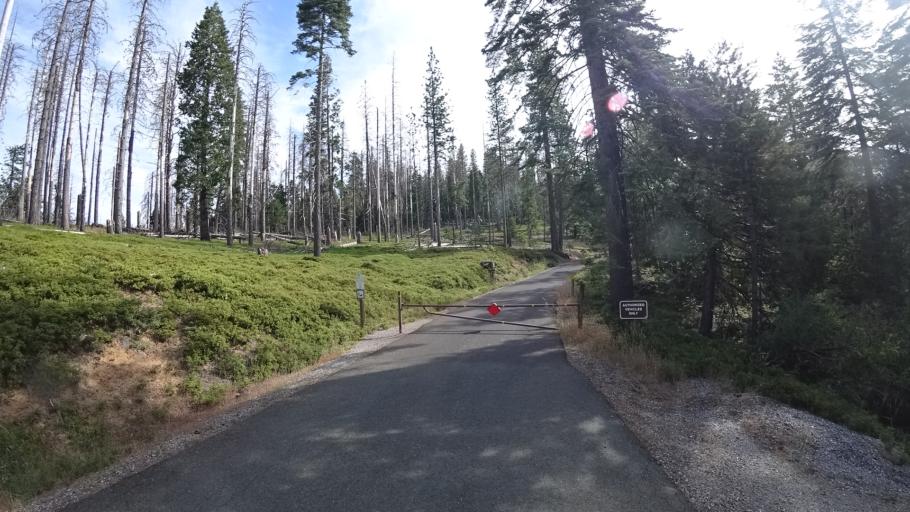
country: US
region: California
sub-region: Calaveras County
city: Arnold
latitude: 38.2672
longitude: -120.3208
